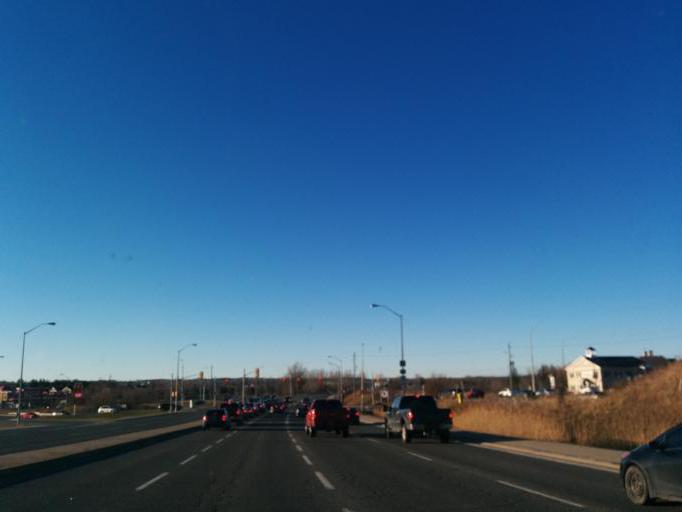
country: CA
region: Ontario
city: Orangeville
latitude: 43.9213
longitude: -80.0817
